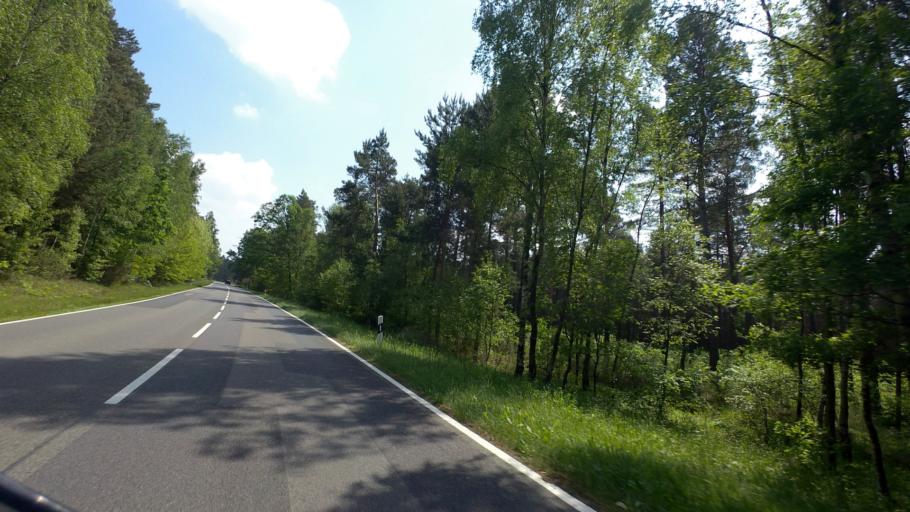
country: DE
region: Saxony
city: Schleife
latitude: 51.5642
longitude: 14.4861
